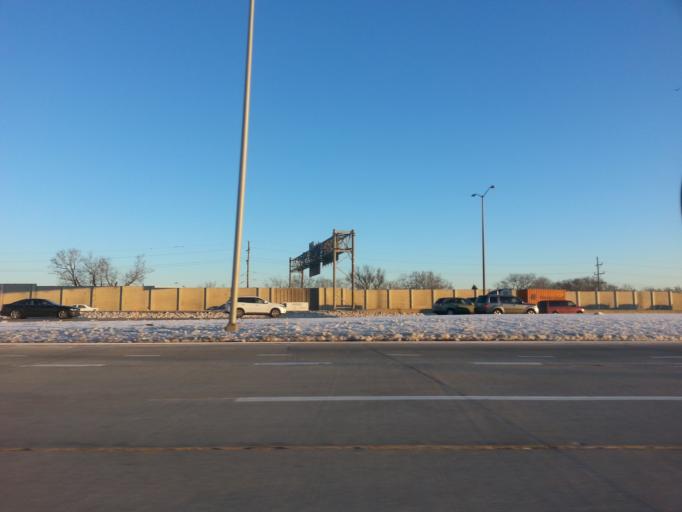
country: US
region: Illinois
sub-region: Cook County
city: Schiller Park
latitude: 41.9647
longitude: -87.8753
